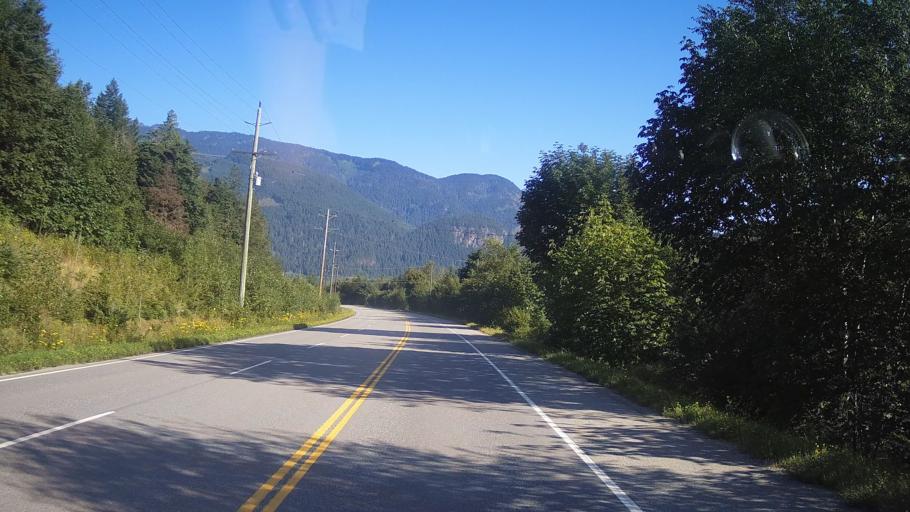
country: CA
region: British Columbia
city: Hope
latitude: 49.5296
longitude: -121.4234
